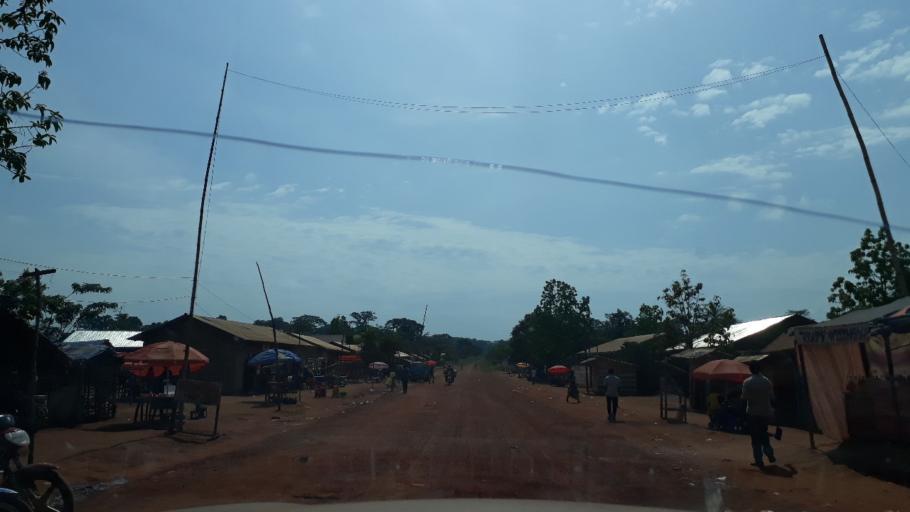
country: CD
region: Eastern Province
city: Wamba
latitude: 1.4095
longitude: 28.0807
